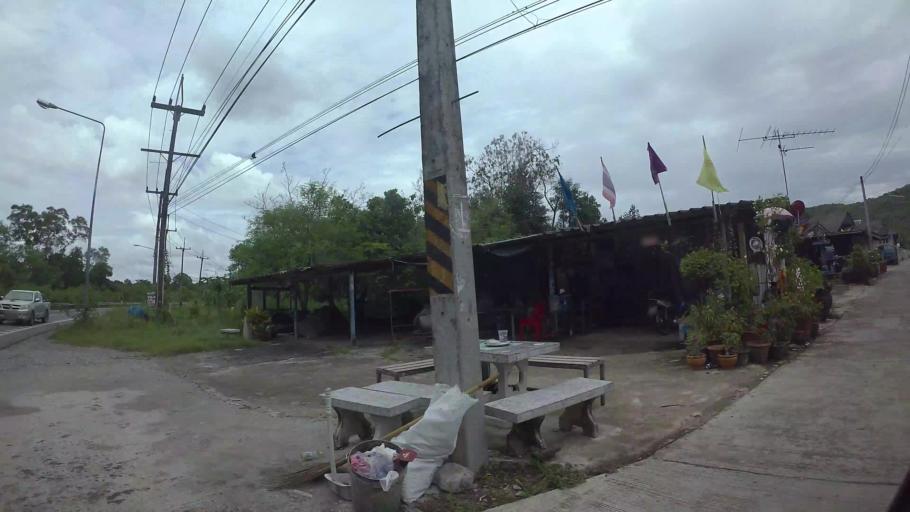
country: TH
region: Chon Buri
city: Si Racha
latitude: 13.1877
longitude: 100.9657
